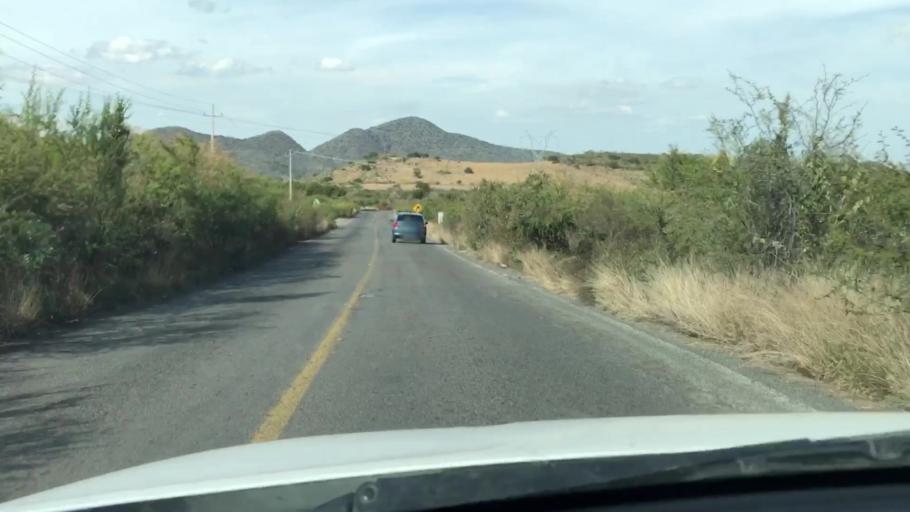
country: MX
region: Jalisco
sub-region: Zacoalco de Torres
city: Barranca de Otates (Barranca de Otatan)
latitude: 20.2346
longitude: -103.6854
